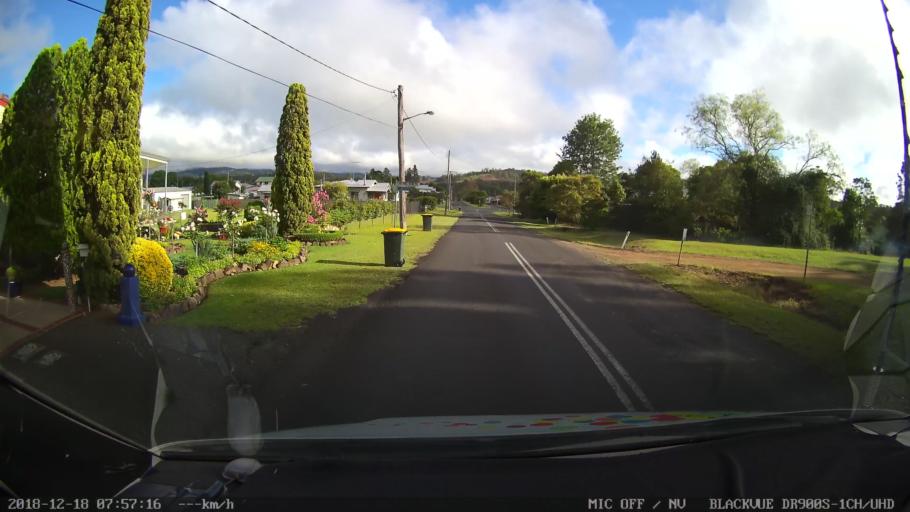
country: AU
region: New South Wales
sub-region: Kyogle
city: Kyogle
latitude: -28.3946
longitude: 152.6113
